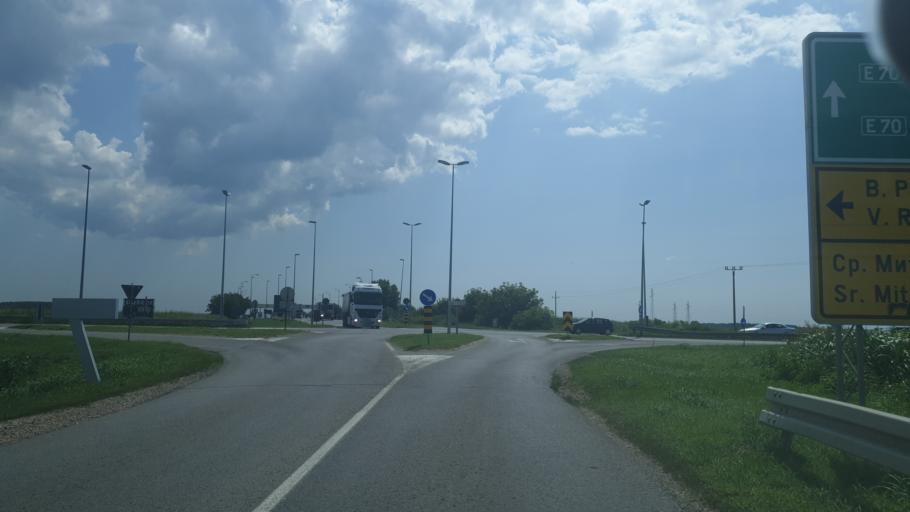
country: RS
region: Autonomna Pokrajina Vojvodina
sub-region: Sremski Okrug
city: Sremska Mitrovica
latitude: 44.9954
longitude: 19.6407
